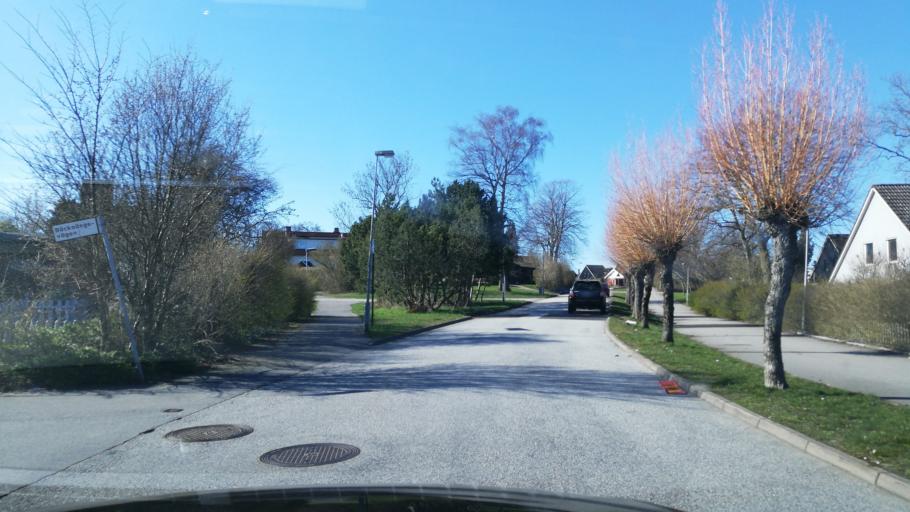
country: SE
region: Skane
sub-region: Malmo
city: Oxie
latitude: 55.5504
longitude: 13.0998
